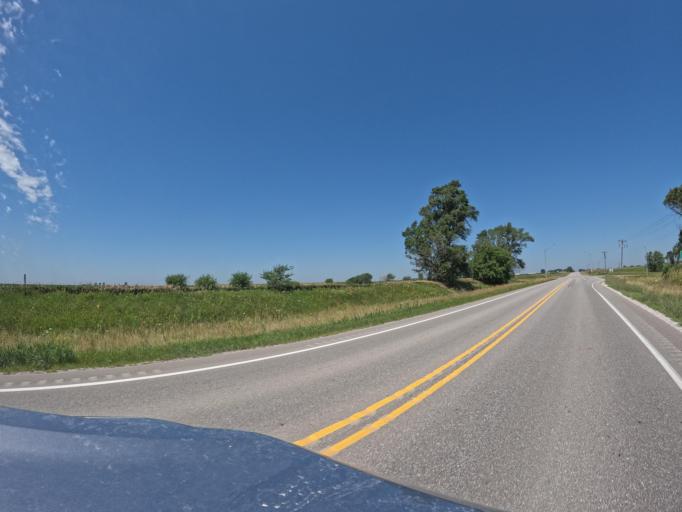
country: US
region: Iowa
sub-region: Keokuk County
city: Sigourney
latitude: 41.4510
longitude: -92.3550
